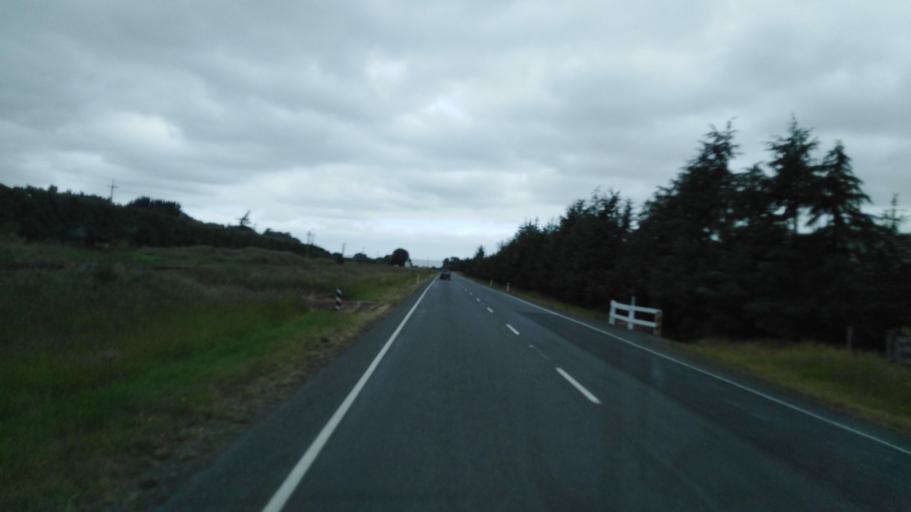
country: NZ
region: Canterbury
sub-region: Hurunui District
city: Amberley
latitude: -42.8943
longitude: 173.1288
